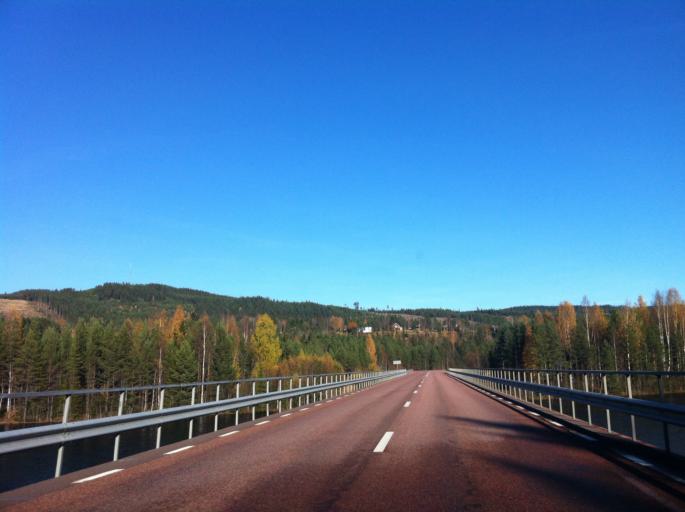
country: SE
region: Dalarna
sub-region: Alvdalens Kommun
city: AElvdalen
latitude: 61.2768
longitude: 13.9304
